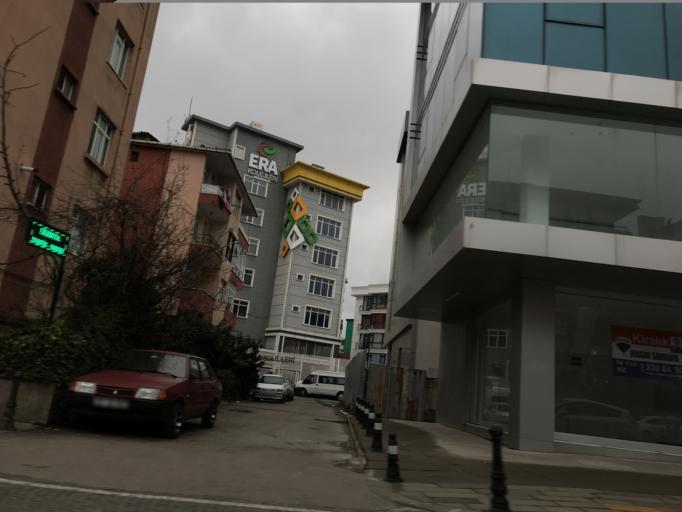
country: TR
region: Istanbul
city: Pendik
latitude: 40.8835
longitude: 29.2350
